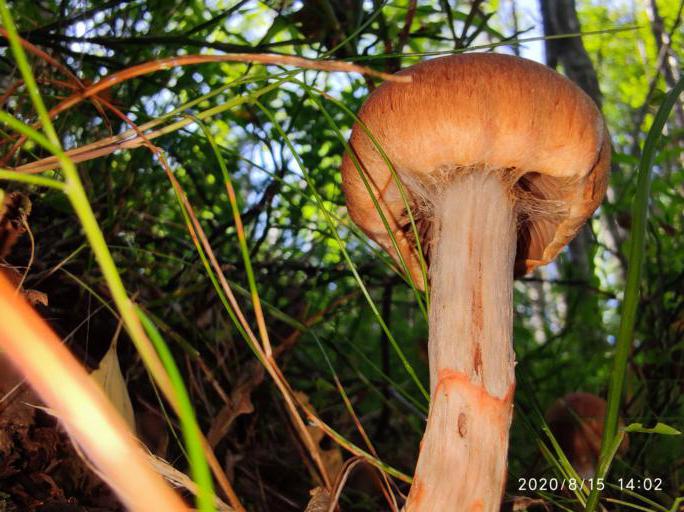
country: NO
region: Akershus
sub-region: Nittedal
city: Rotnes
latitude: 60.0628
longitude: 10.8487
